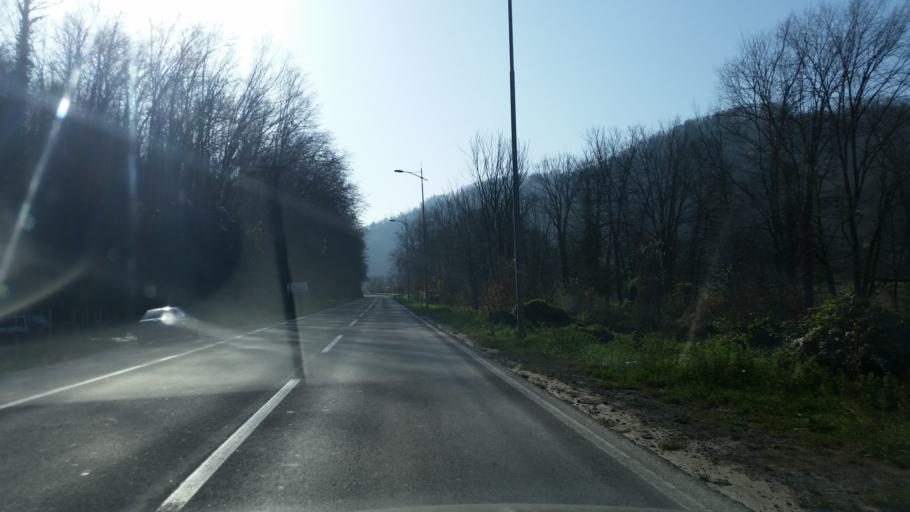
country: RS
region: Central Serbia
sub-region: Kolubarski Okrug
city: Ljig
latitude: 44.2112
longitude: 20.2259
